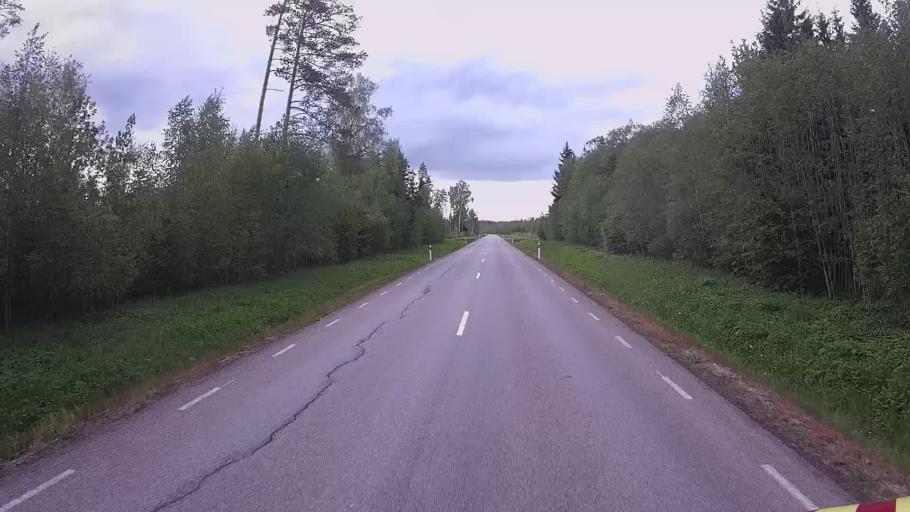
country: EE
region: Jogevamaa
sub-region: Mustvee linn
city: Mustvee
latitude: 59.0758
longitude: 26.9955
